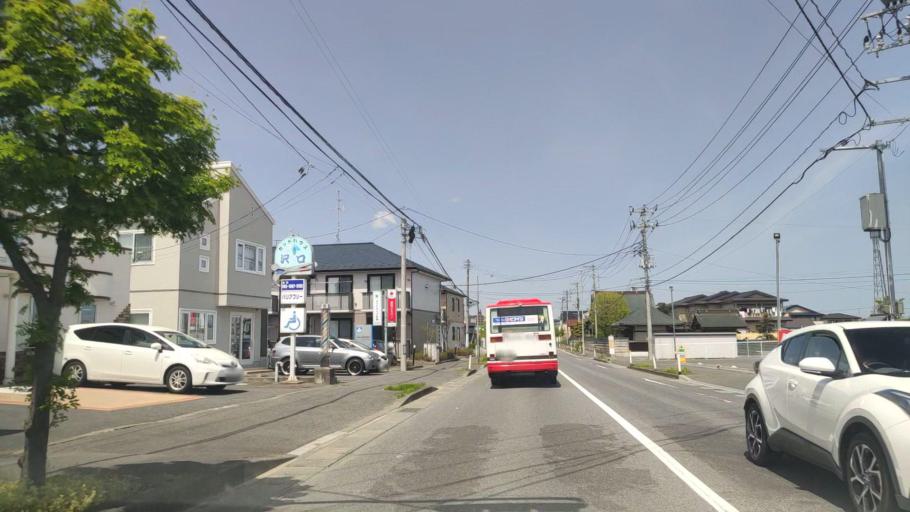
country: JP
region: Aomori
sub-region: Hachinohe Shi
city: Uchimaru
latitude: 40.5040
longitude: 141.4397
